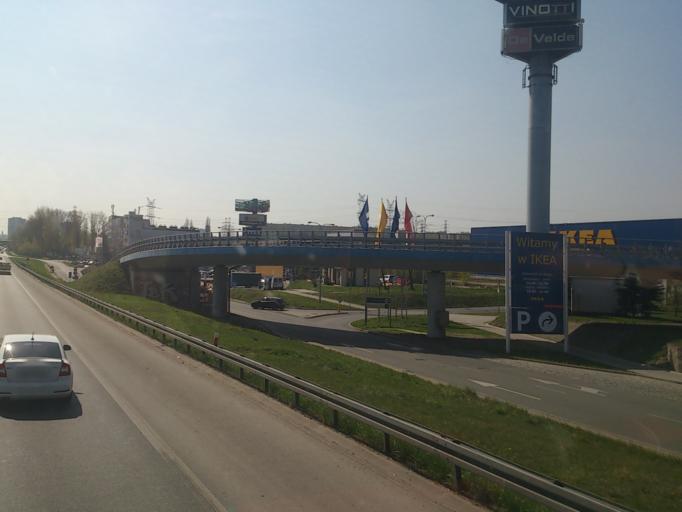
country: PL
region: Silesian Voivodeship
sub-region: Katowice
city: Katowice
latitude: 50.2697
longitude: 19.0599
